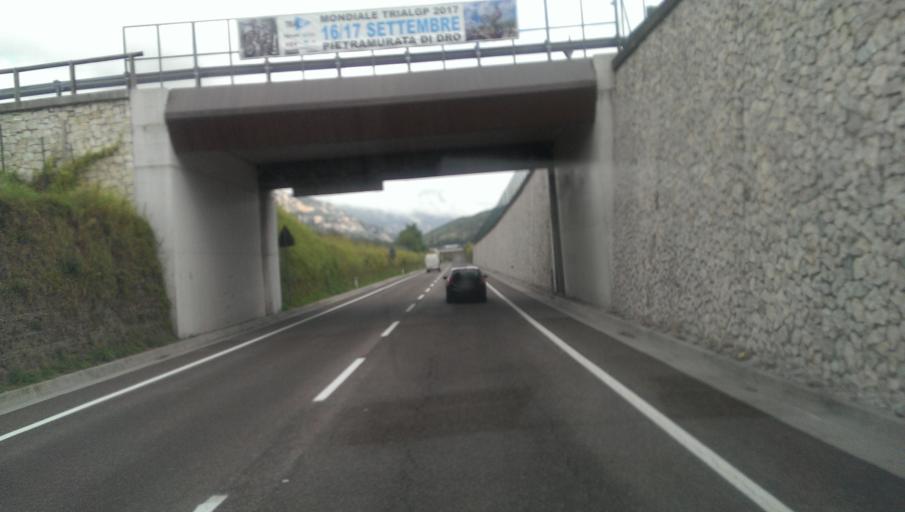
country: IT
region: Trentino-Alto Adige
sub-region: Provincia di Trento
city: Arco
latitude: 45.9160
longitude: 10.8957
